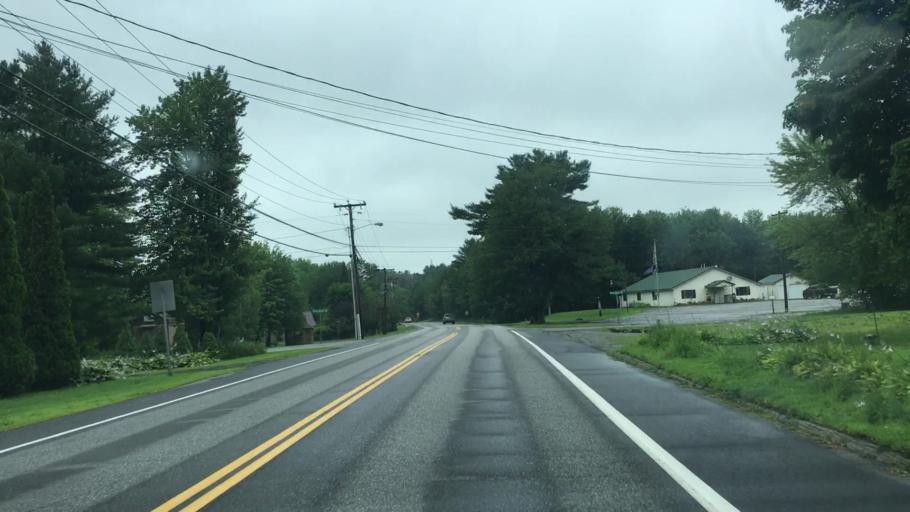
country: US
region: Maine
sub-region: Kennebec County
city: Augusta
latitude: 44.3454
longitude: -69.8061
